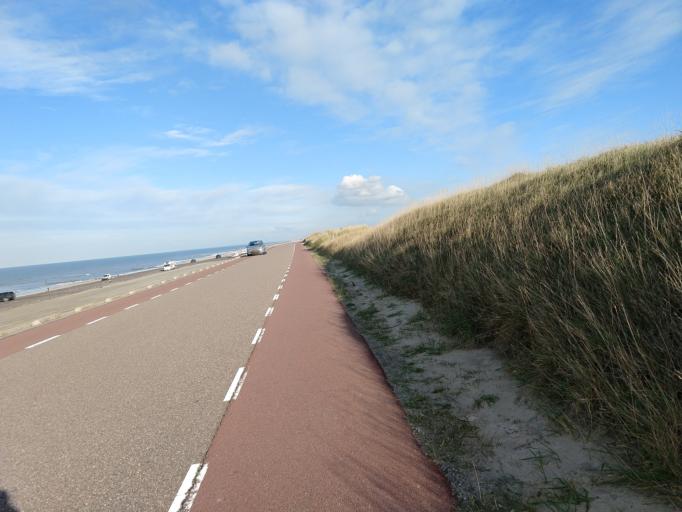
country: NL
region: Zeeland
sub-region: Gemeente Vlissingen
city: Vlissingen
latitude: 51.5462
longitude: 3.4505
